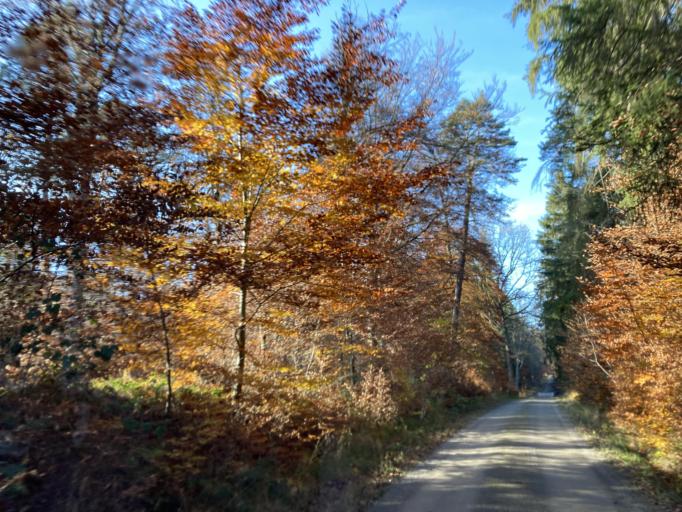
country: DE
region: Baden-Wuerttemberg
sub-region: Regierungsbezirk Stuttgart
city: Altdorf
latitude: 48.5704
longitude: 9.0093
